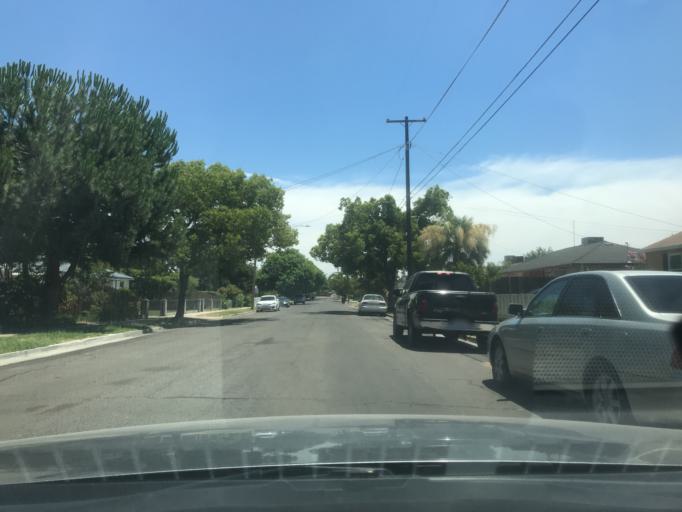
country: US
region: California
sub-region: Merced County
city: Atwater
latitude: 37.3442
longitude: -120.5991
